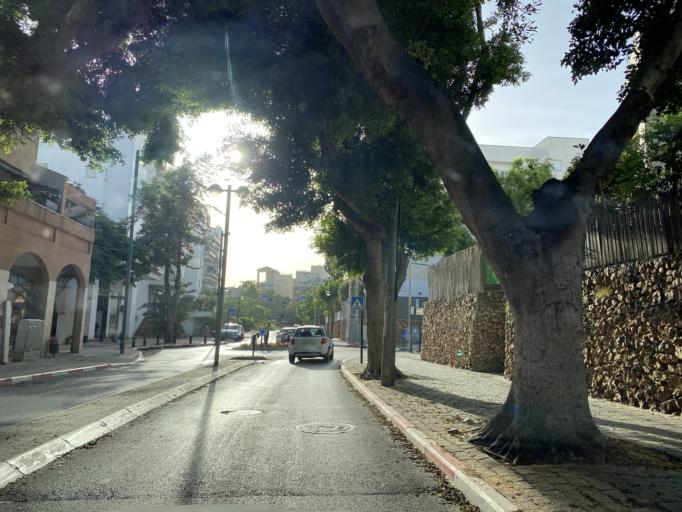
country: IL
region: Central District
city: Kfar Saba
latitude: 32.1786
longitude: 34.9071
